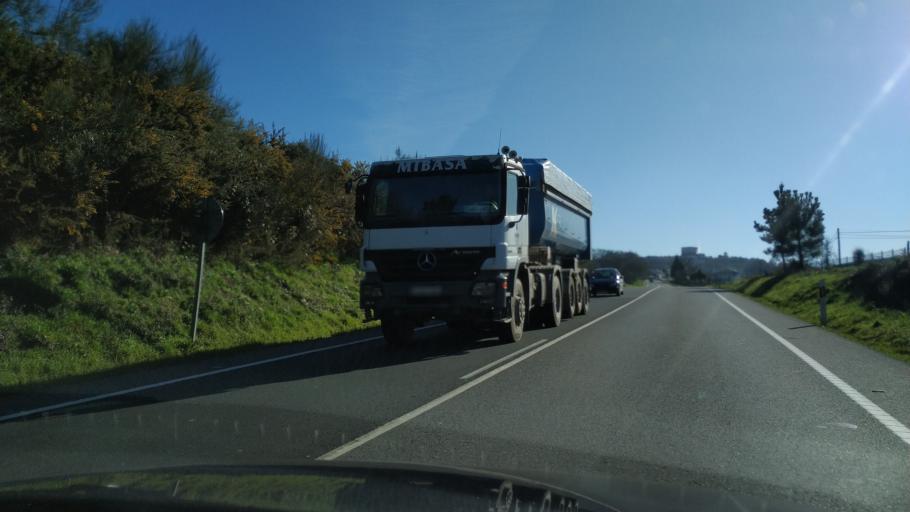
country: ES
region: Galicia
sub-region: Provincia de Pontevedra
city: Silleda
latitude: 42.7097
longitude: -8.2725
